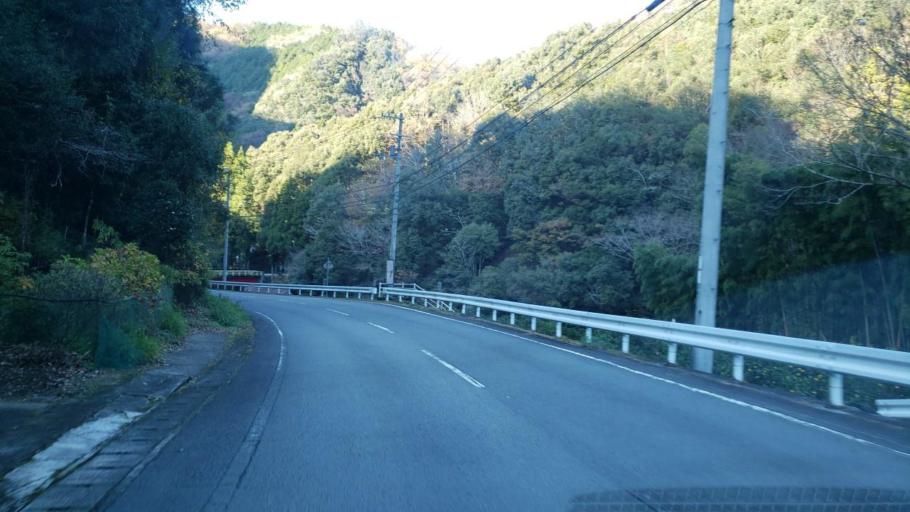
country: JP
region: Tokushima
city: Wakimachi
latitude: 34.0094
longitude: 134.0323
